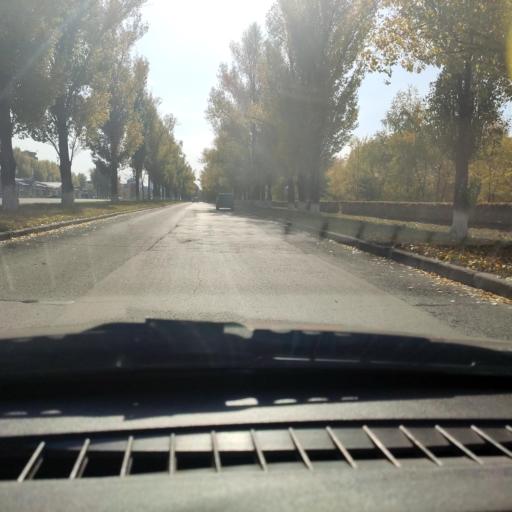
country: RU
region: Samara
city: Tol'yatti
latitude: 53.5245
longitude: 49.2801
